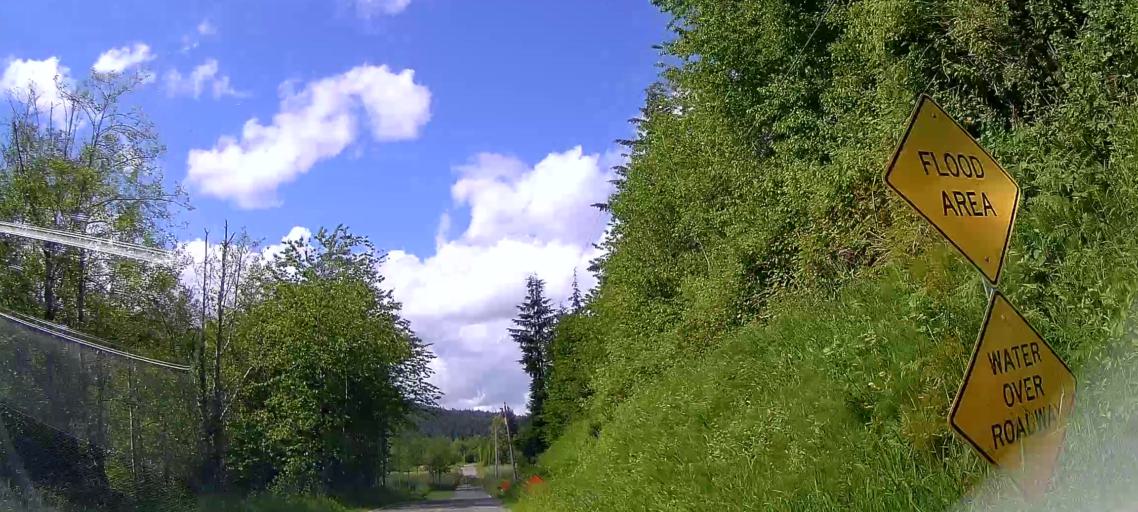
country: US
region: Washington
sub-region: Whatcom County
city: Sudden Valley
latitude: 48.6702
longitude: -122.1950
